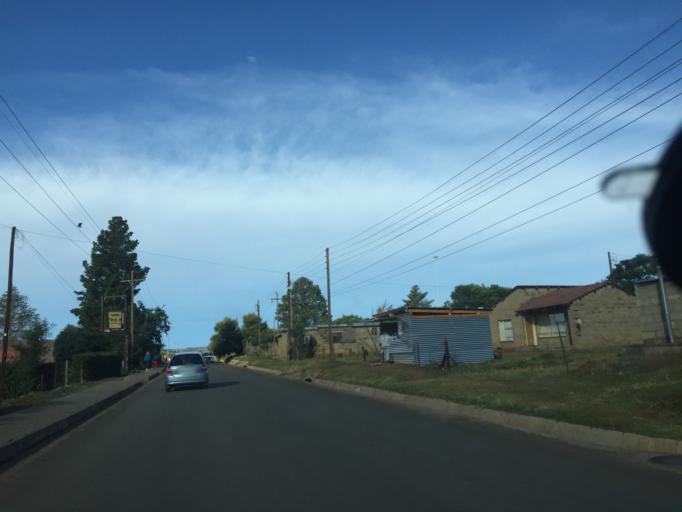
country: LS
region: Maseru
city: Maseru
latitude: -29.2885
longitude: 27.5316
